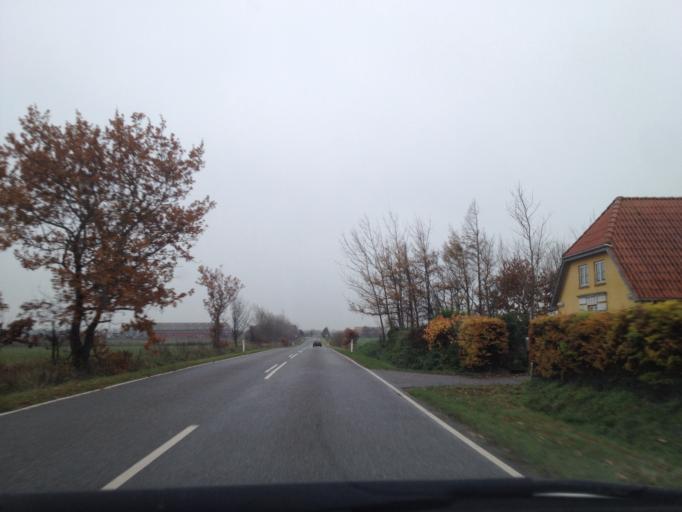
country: DK
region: South Denmark
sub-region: Tonder Kommune
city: Sherrebek
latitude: 55.0762
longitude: 8.7268
